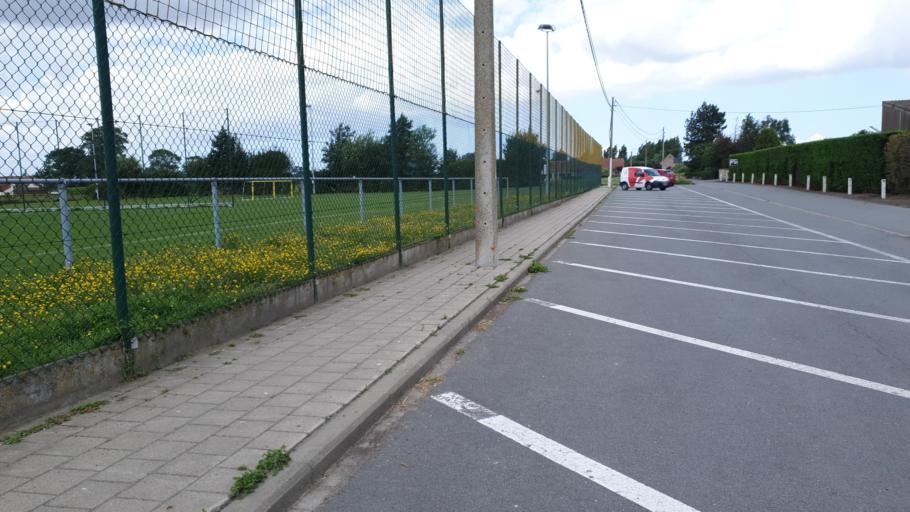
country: BE
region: Flanders
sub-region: Provincie West-Vlaanderen
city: Alveringem
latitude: 51.0156
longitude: 2.7114
